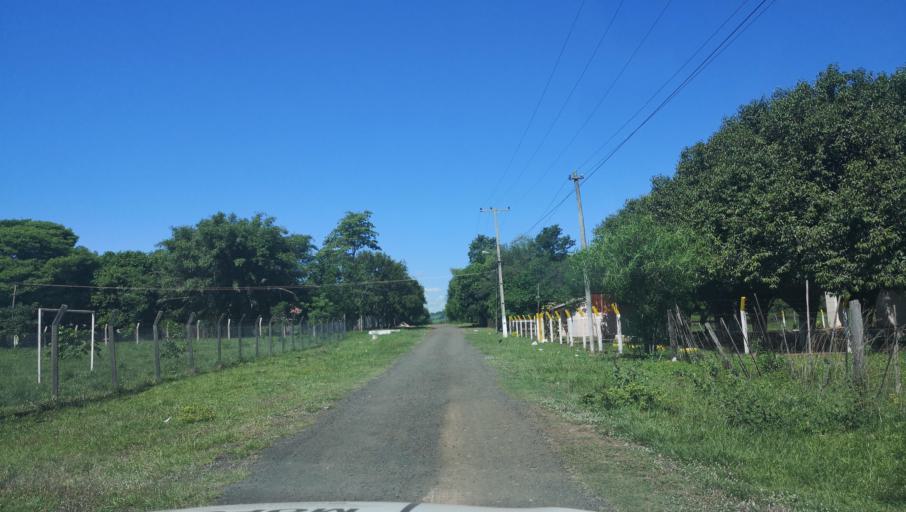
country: PY
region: Caaguazu
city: Carayao
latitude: -25.2057
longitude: -56.4015
